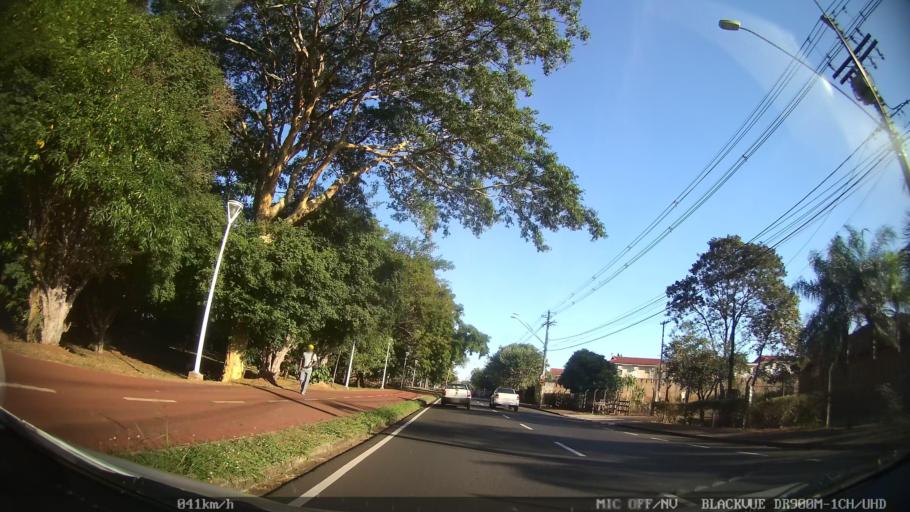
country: BR
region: Sao Paulo
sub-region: Sao Jose Do Rio Preto
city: Sao Jose do Rio Preto
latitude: -20.8475
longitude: -49.4130
